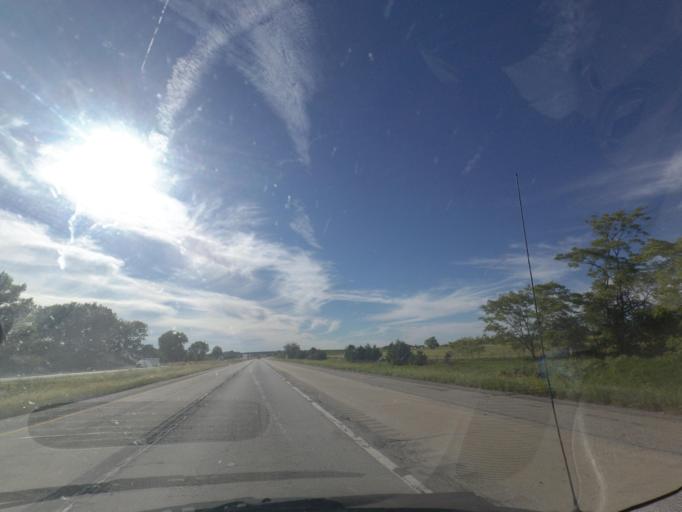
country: US
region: Illinois
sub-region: Macon County
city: Forsyth
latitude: 39.9079
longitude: -88.9696
